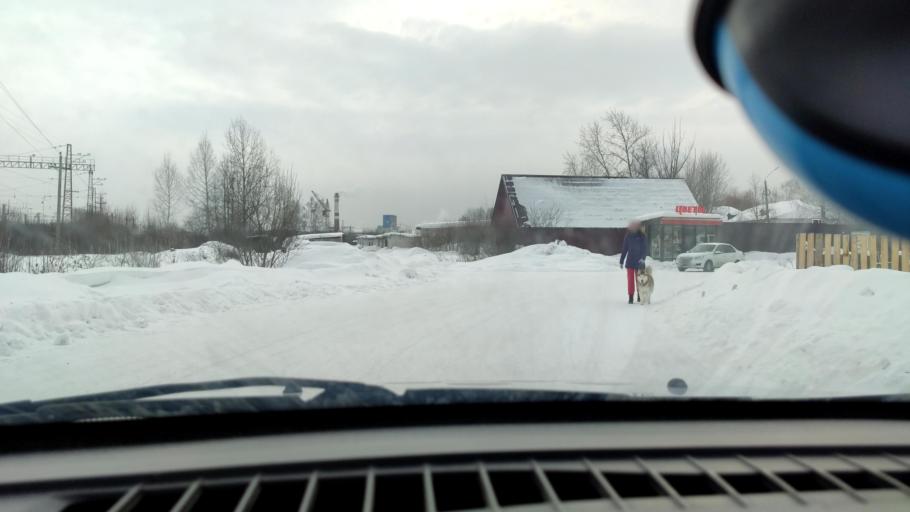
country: RU
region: Perm
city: Overyata
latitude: 58.0809
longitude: 55.8730
